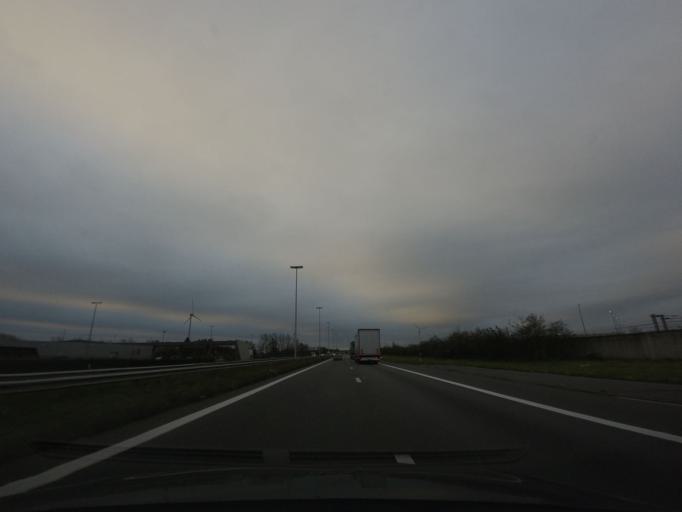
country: BE
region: Flanders
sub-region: Provincie Antwerpen
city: Hoogstraten
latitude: 51.4211
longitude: 4.7065
